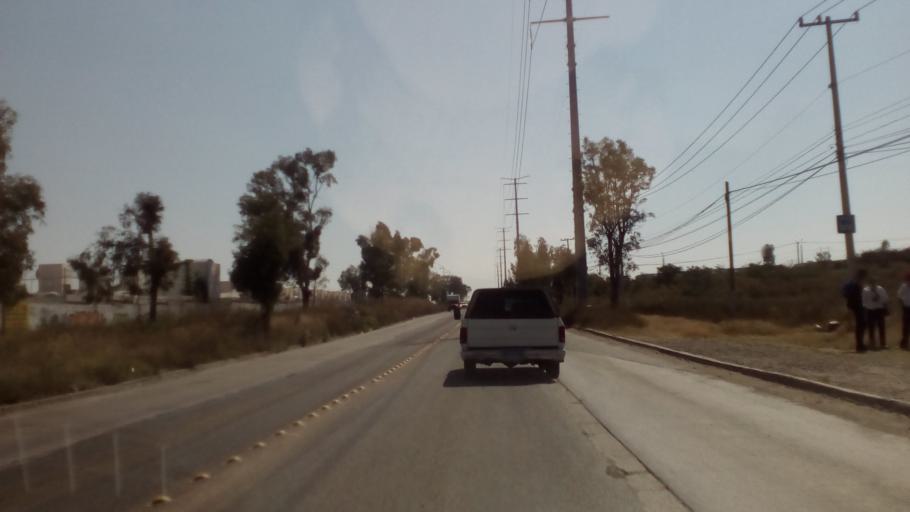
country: MX
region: Guanajuato
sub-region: Leon
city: La Ermita
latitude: 21.1707
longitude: -101.7376
